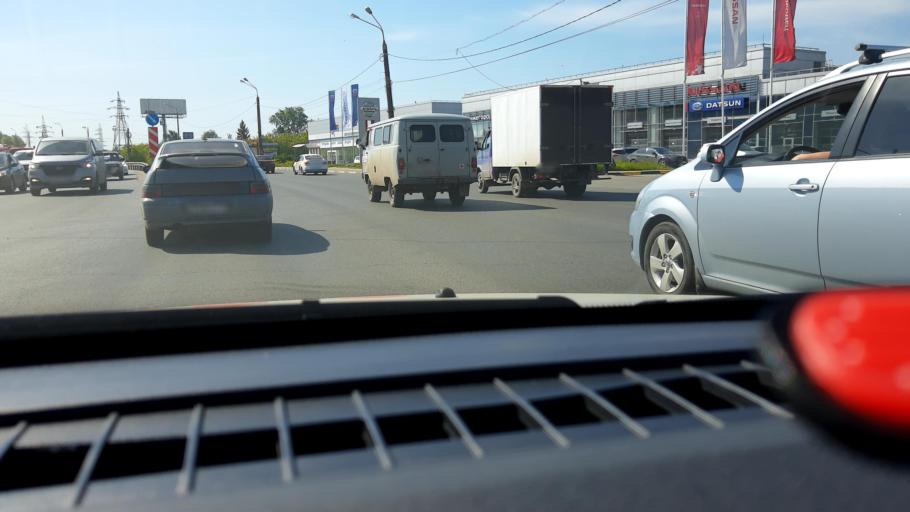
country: RU
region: Nizjnij Novgorod
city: Nizhniy Novgorod
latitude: 56.3103
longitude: 43.8985
